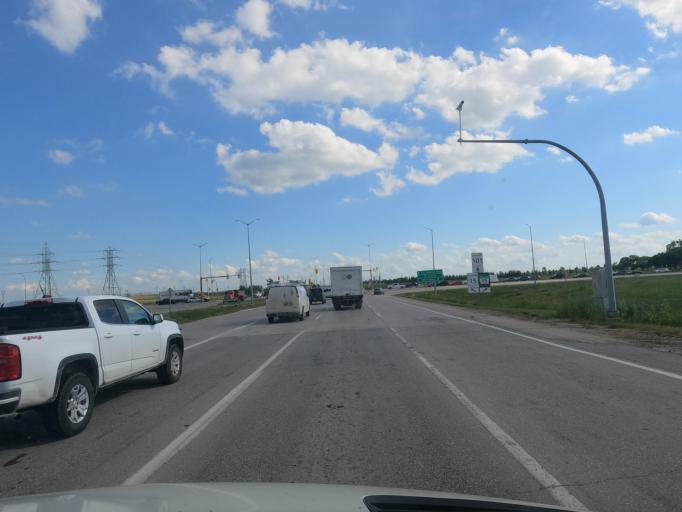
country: CA
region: Manitoba
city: Winnipeg
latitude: 49.8874
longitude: -96.9591
